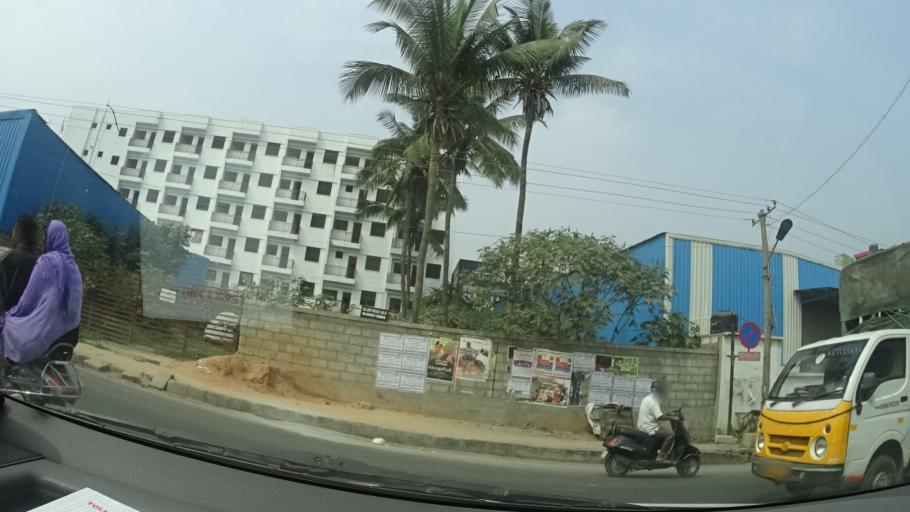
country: IN
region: Karnataka
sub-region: Bangalore Urban
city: Bangalore
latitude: 13.0220
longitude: 77.6195
